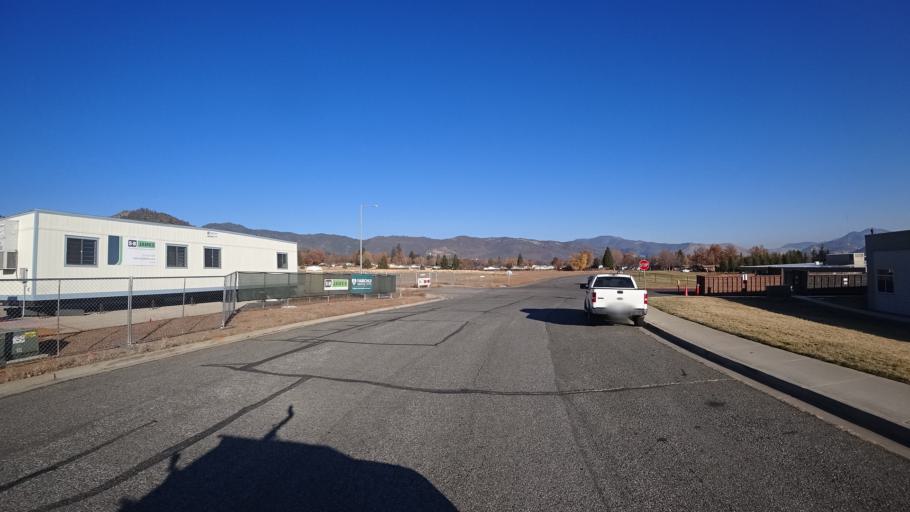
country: US
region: California
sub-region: Siskiyou County
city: Yreka
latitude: 41.7183
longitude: -122.6472
